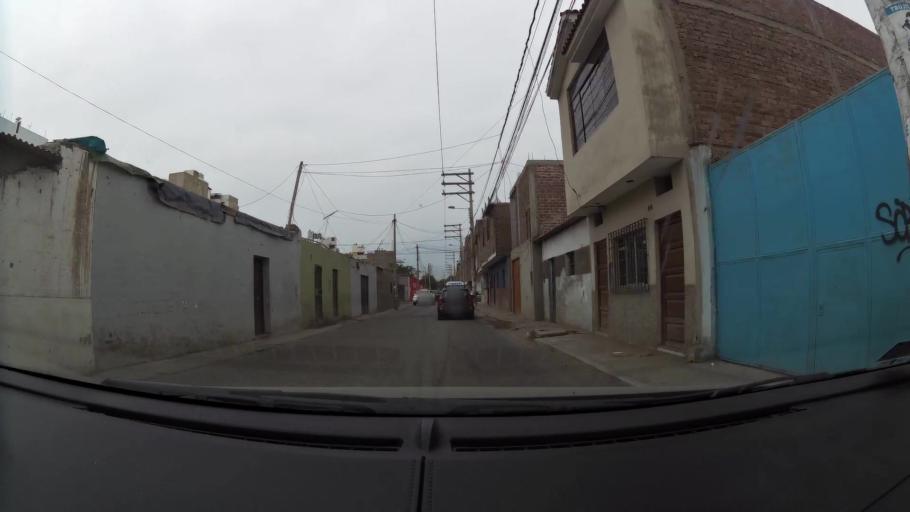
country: PE
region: La Libertad
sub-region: Provincia de Trujillo
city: Buenos Aires
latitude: -8.1368
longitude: -79.0397
